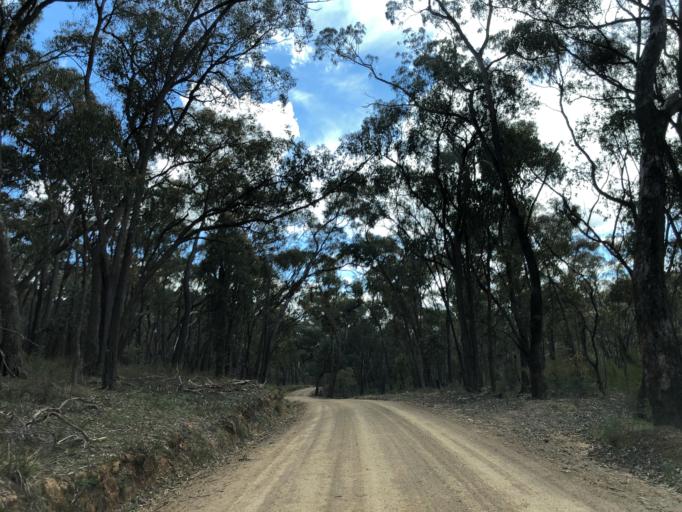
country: AU
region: Victoria
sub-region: Benalla
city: Benalla
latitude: -36.7435
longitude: 146.1574
